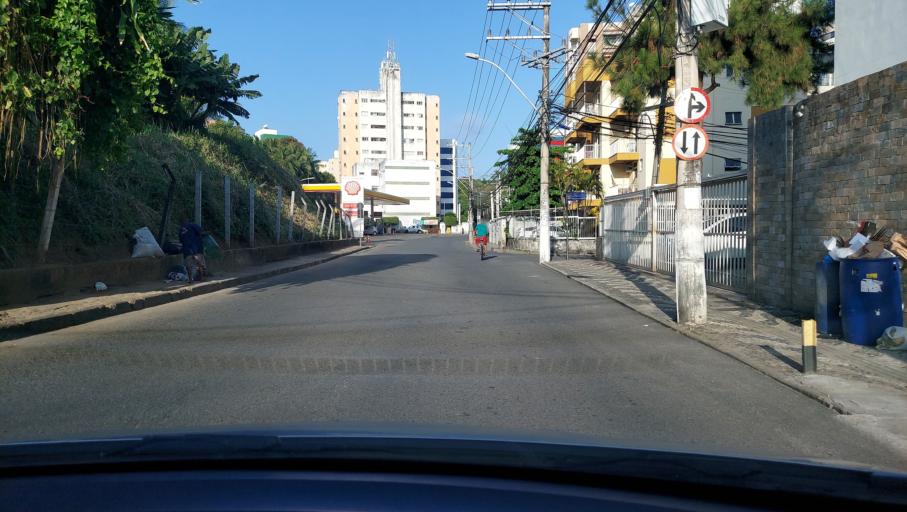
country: BR
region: Bahia
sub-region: Salvador
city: Salvador
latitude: -12.9888
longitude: -38.4476
